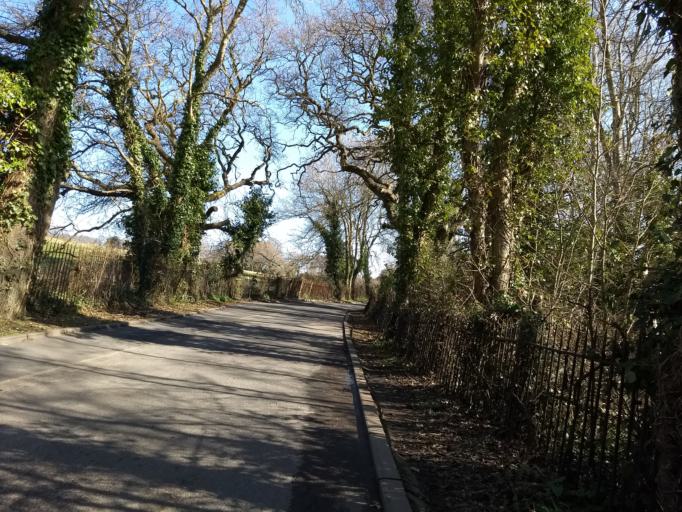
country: GB
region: England
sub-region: Isle of Wight
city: Seaview
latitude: 50.7035
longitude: -1.1075
